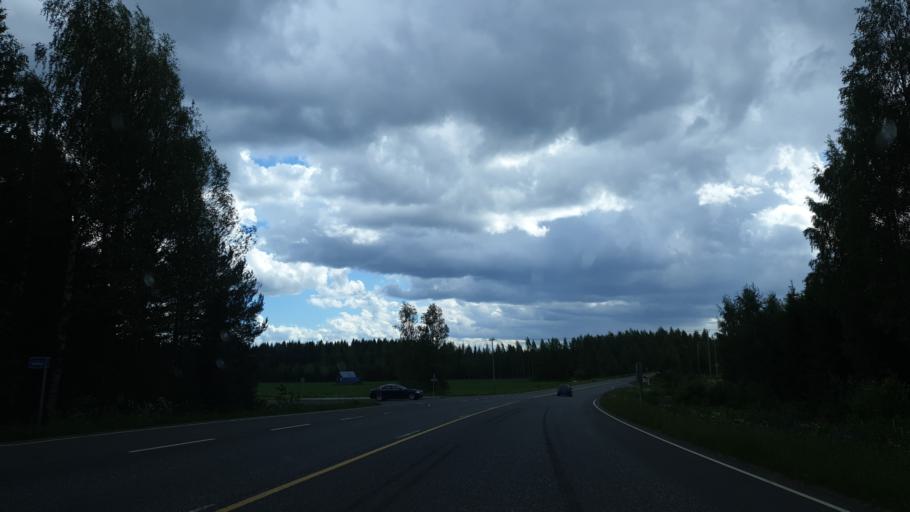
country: FI
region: Northern Savo
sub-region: Koillis-Savo
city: Kaavi
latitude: 62.9520
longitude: 28.4011
